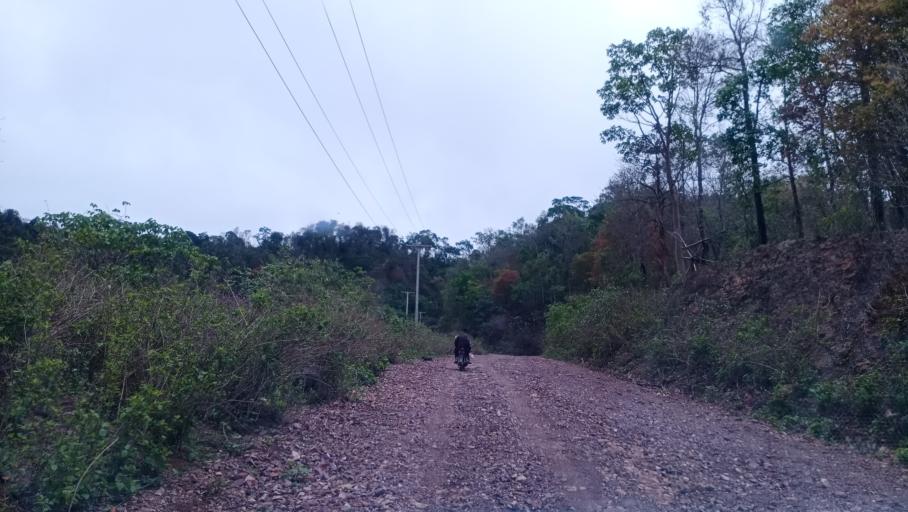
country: LA
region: Phongsali
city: Phongsali
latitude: 21.3464
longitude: 102.0949
